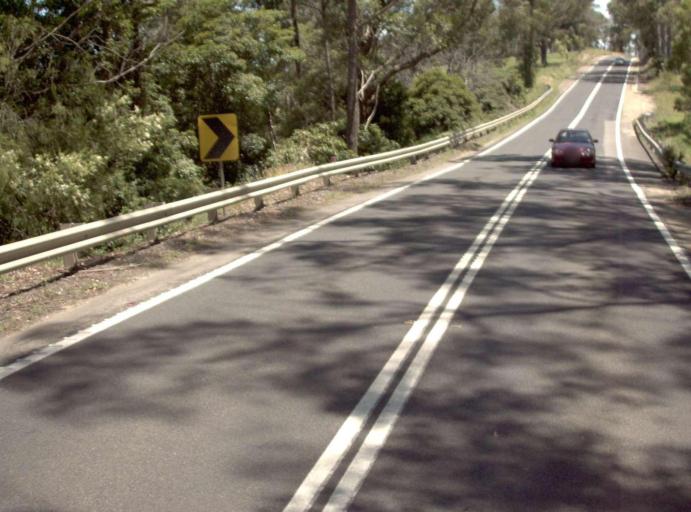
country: AU
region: Victoria
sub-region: East Gippsland
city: Lakes Entrance
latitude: -37.7051
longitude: 148.5535
